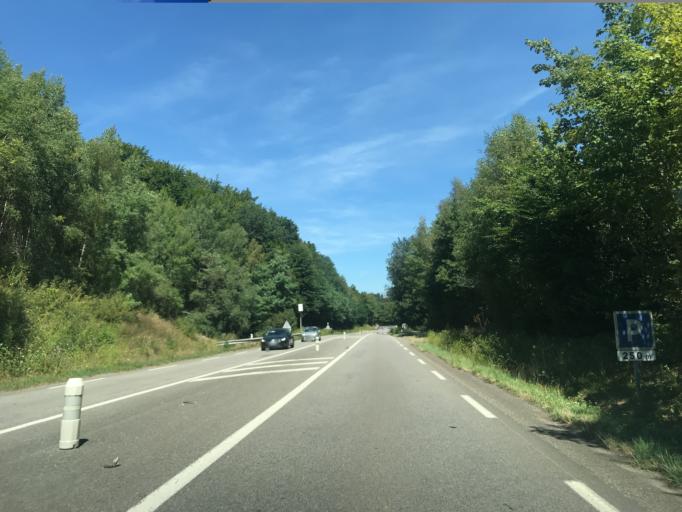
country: FR
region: Limousin
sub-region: Departement de la Correze
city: Naves
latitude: 45.2915
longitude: 1.8075
